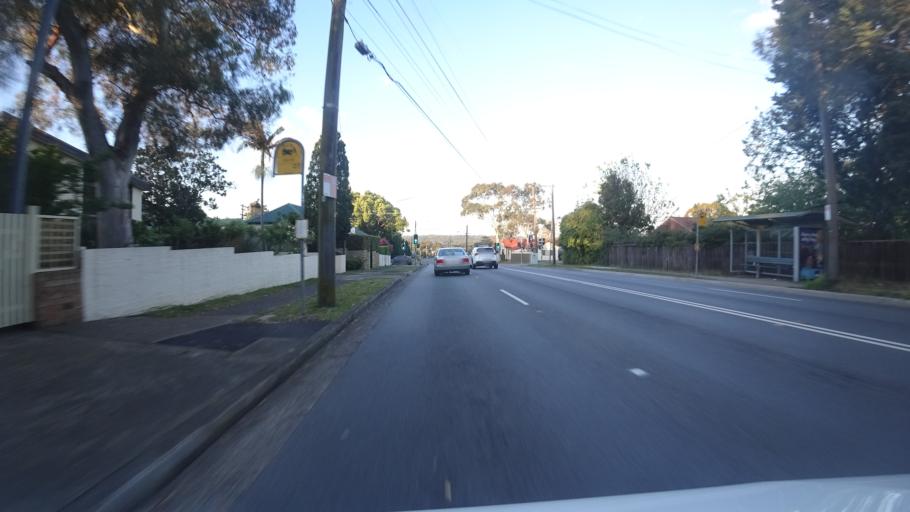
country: AU
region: New South Wales
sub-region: Ryde
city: North Ryde
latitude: -33.7973
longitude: 151.1239
